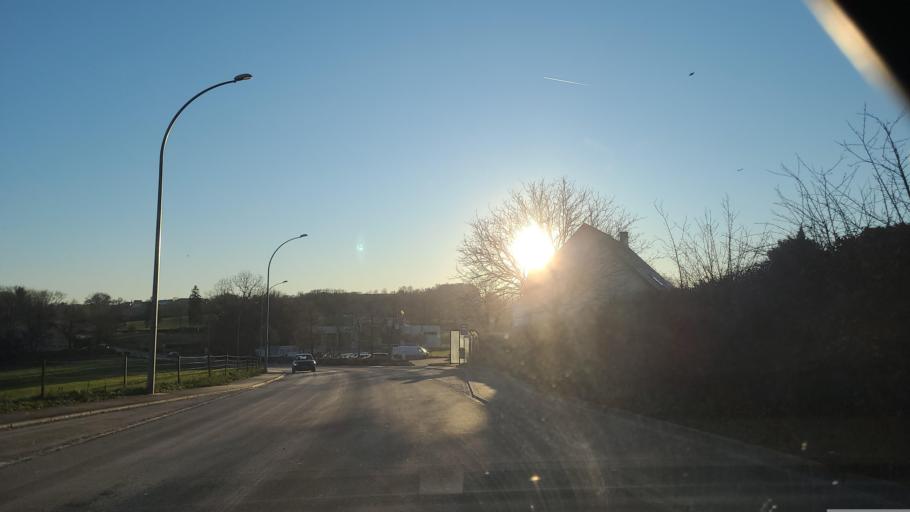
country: LU
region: Luxembourg
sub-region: Canton de Capellen
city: Garnich
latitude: 49.6138
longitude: 5.9500
